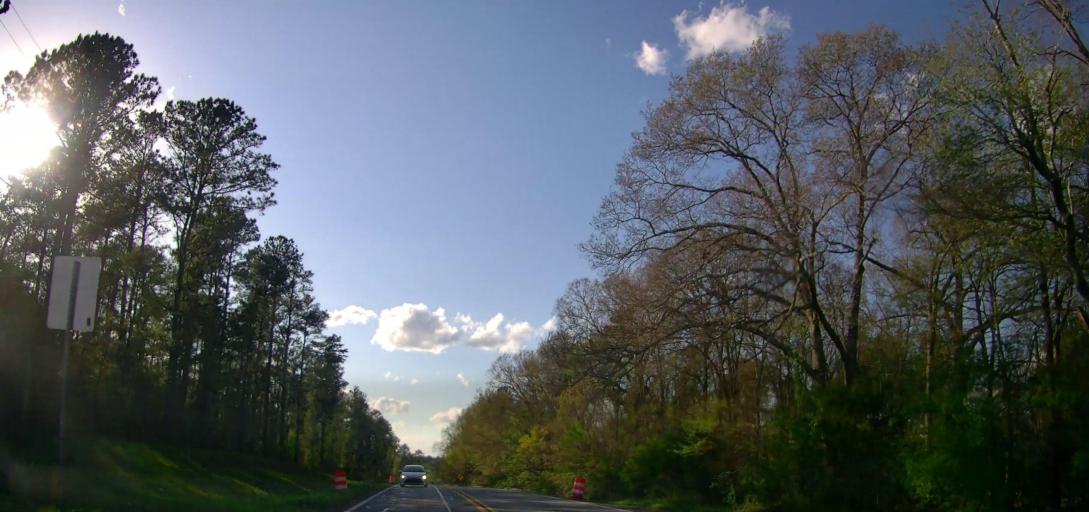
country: US
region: Georgia
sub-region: Baldwin County
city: Milledgeville
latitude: 33.1075
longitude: -83.2800
